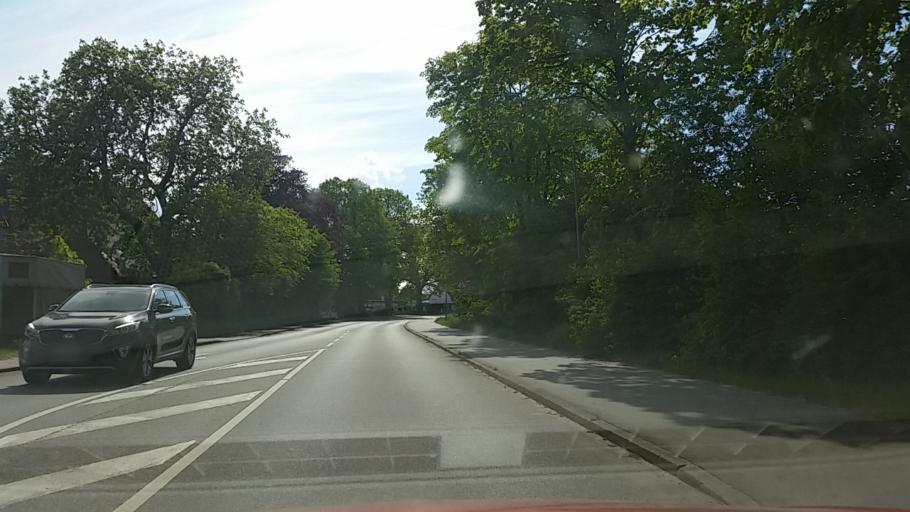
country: DE
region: Schleswig-Holstein
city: Reinfeld
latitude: 53.8276
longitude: 10.5126
